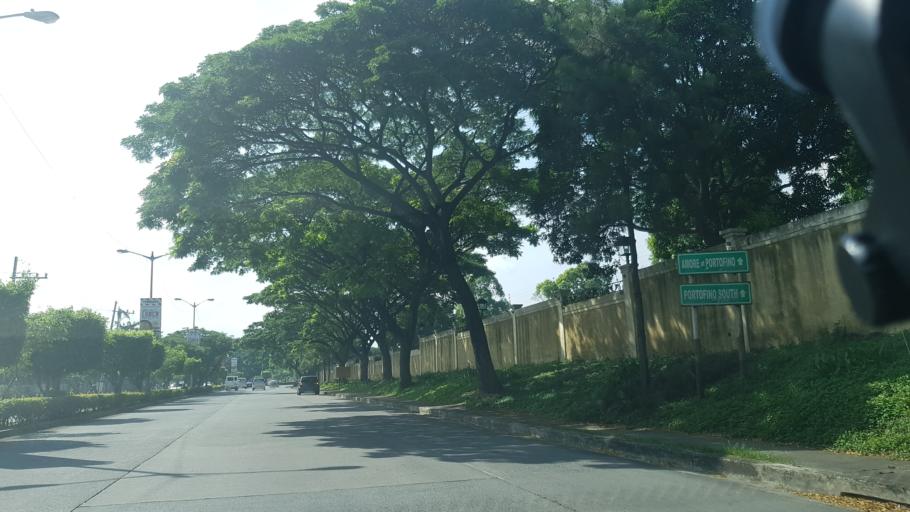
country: PH
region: Calabarzon
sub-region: Province of Laguna
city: San Pedro
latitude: 14.3819
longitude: 121.0123
